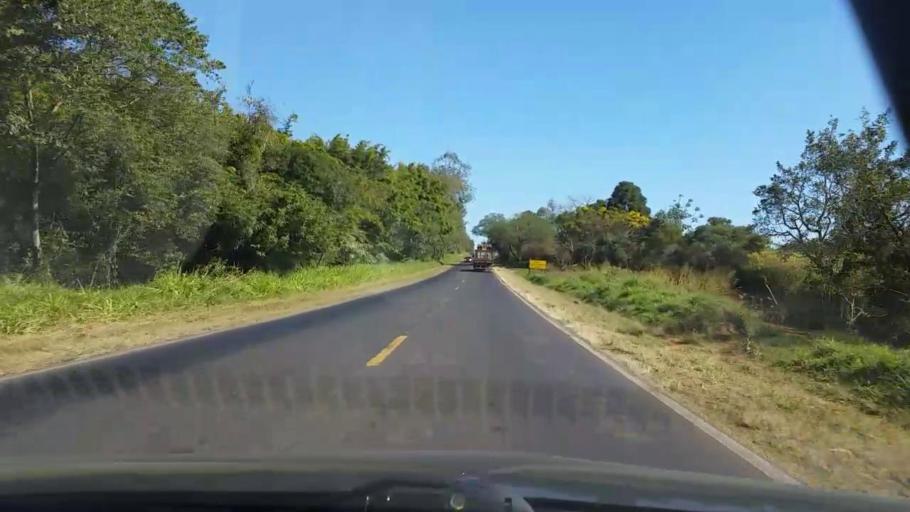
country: BR
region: Sao Paulo
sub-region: Sao Manuel
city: Sao Manuel
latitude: -22.8096
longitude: -48.6751
